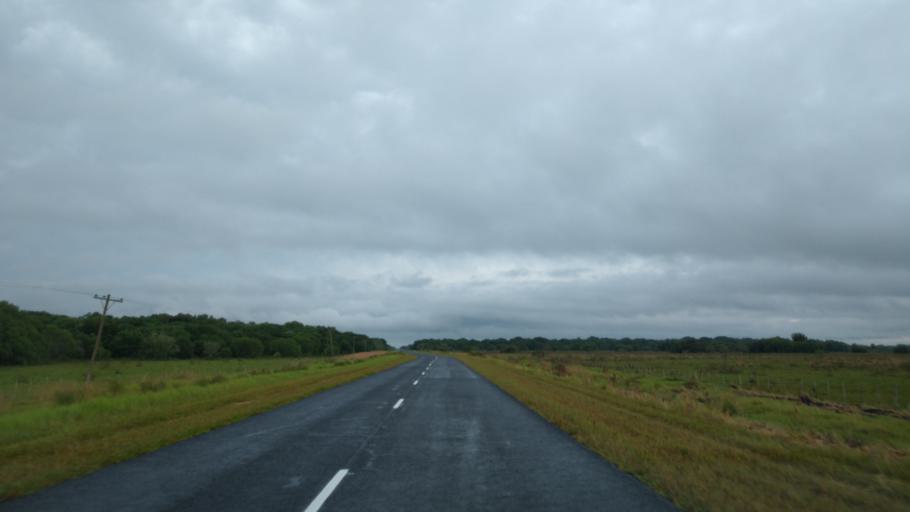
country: AR
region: Corrientes
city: Loreto
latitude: -27.7540
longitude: -57.2580
